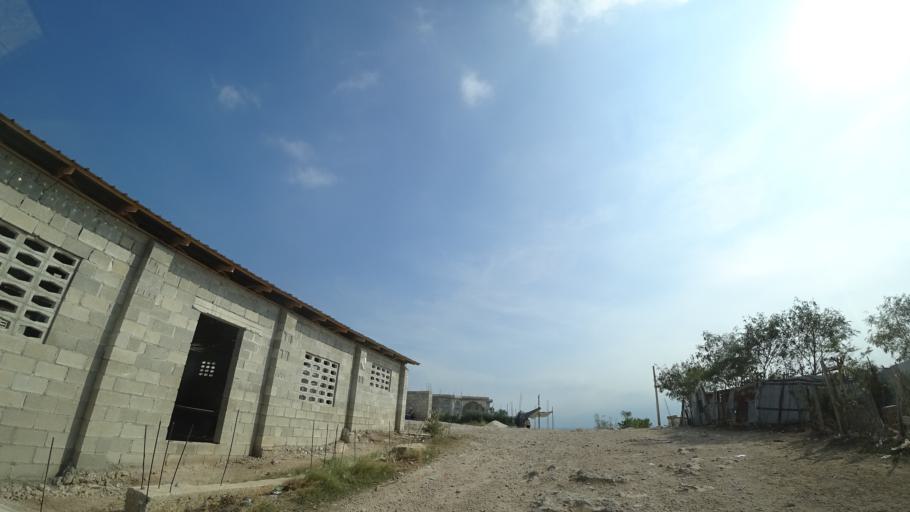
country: HT
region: Ouest
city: Croix des Bouquets
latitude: 18.6626
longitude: -72.2826
